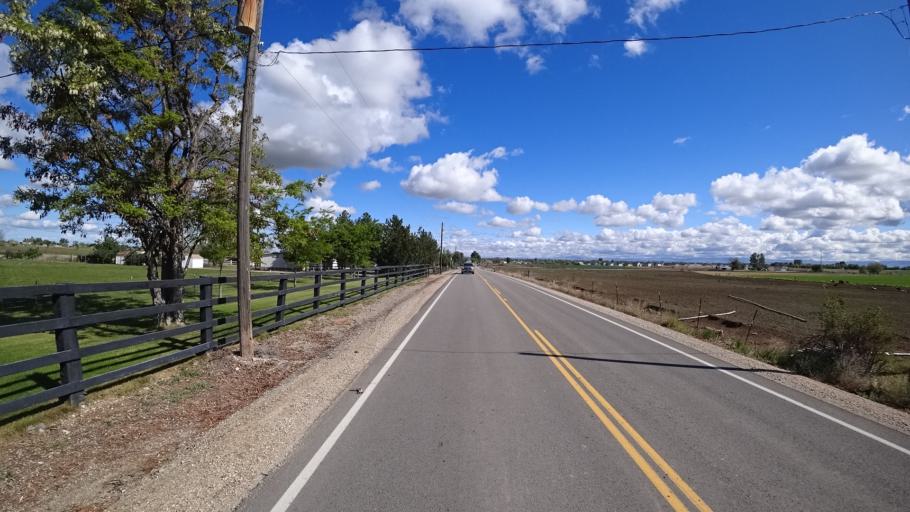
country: US
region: Idaho
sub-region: Ada County
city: Kuna
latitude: 43.4961
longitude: -116.4537
